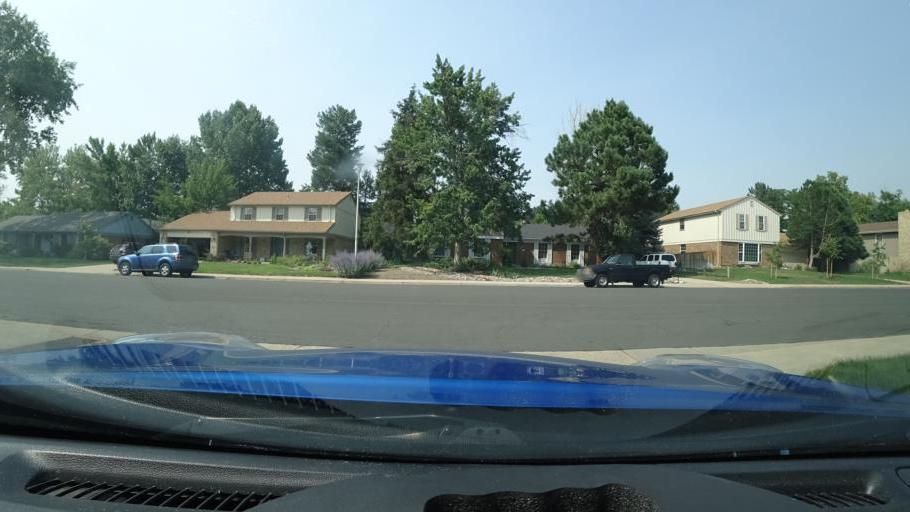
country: US
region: Colorado
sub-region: Adams County
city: Aurora
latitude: 39.6670
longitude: -104.8535
